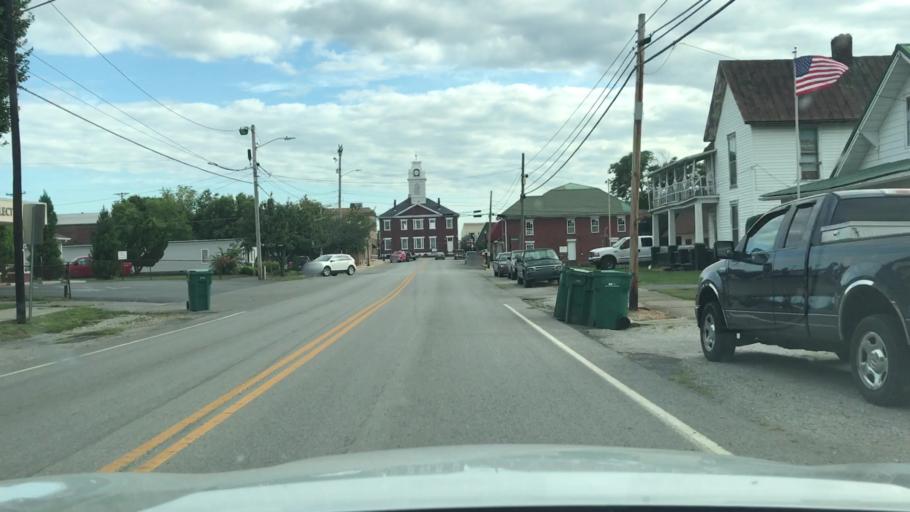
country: US
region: Kentucky
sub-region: Todd County
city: Elkton
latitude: 36.8076
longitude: -87.1546
